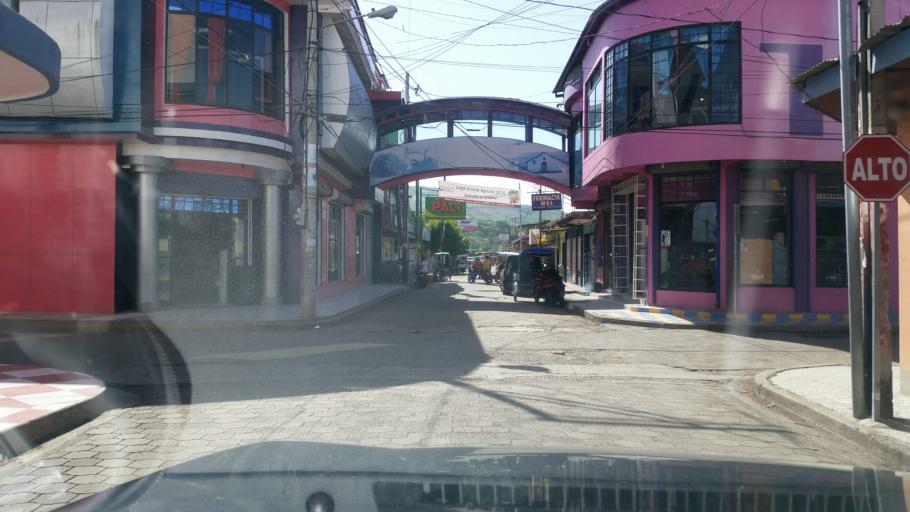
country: NI
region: Matagalpa
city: Ciudad Dario
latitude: 12.8508
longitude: -86.0980
